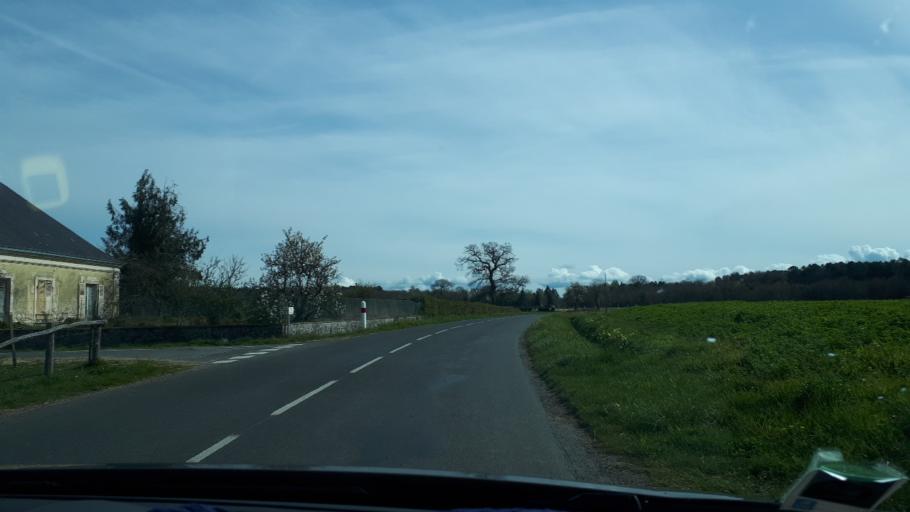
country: FR
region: Pays de la Loire
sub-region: Departement de la Sarthe
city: Yvre-le-Polin
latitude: 47.8160
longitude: 0.1308
